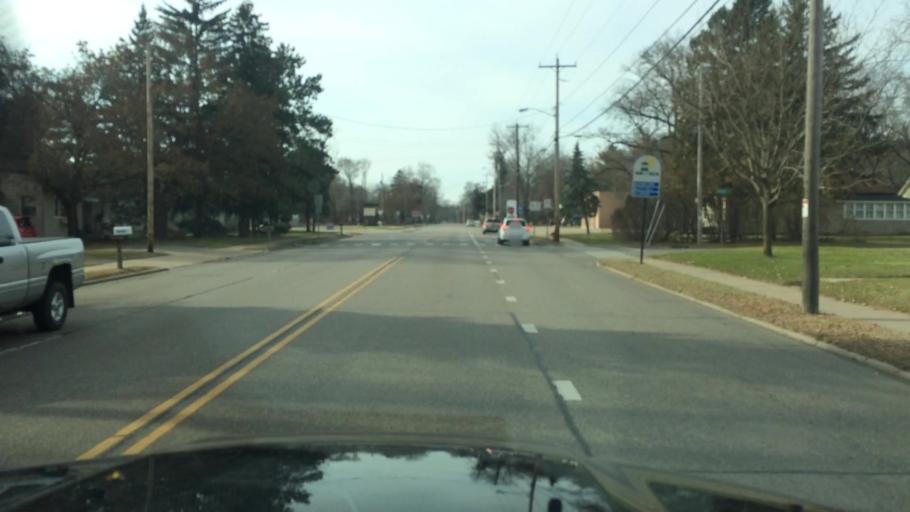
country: US
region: Wisconsin
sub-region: Waupaca County
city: Waupaca
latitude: 44.3514
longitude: -89.0707
